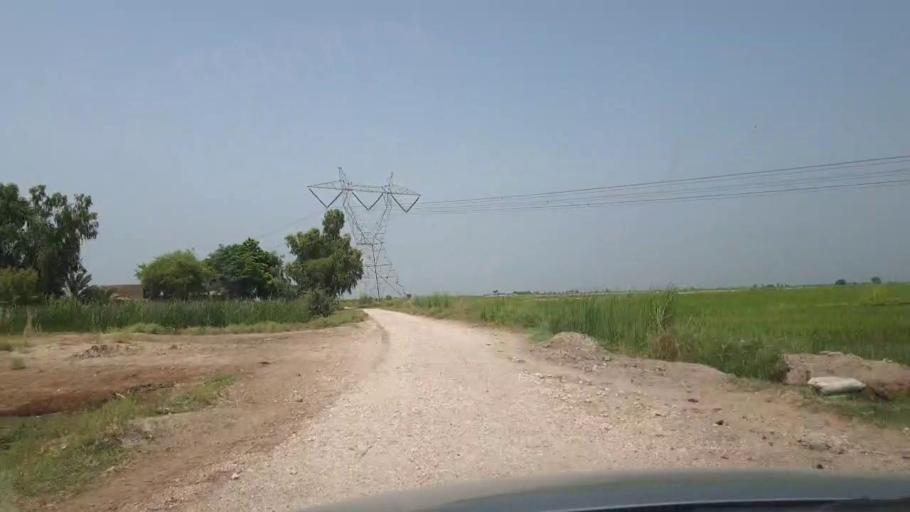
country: PK
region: Sindh
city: Madeji
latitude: 27.8124
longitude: 68.5191
